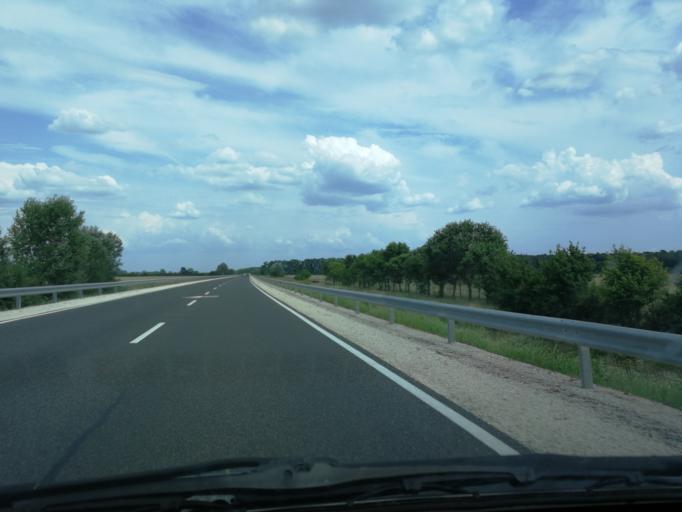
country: HU
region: Bacs-Kiskun
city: Dusnok
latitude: 46.3529
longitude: 18.9194
